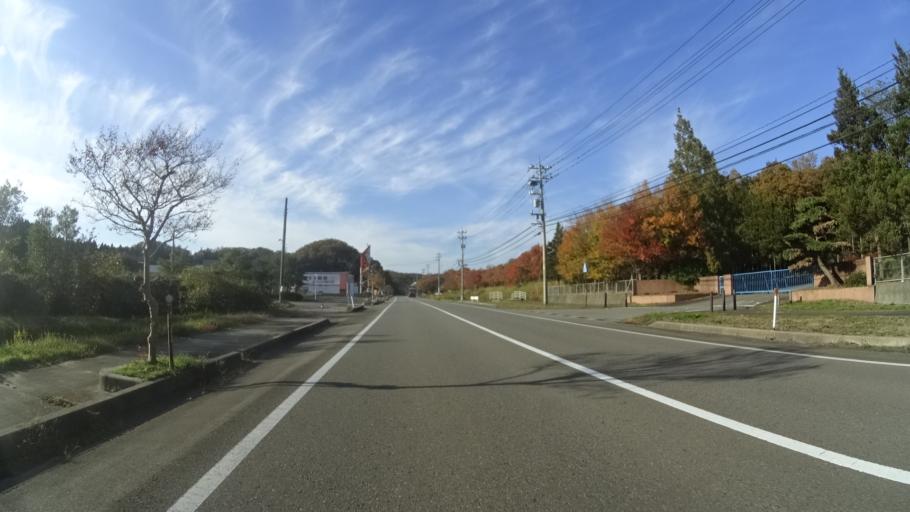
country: JP
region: Ishikawa
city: Hakui
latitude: 37.0255
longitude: 136.7839
